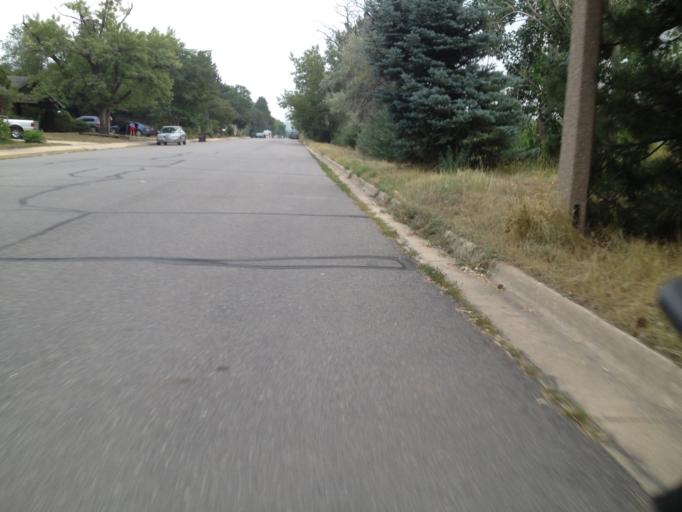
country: US
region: Colorado
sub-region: Boulder County
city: Boulder
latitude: 39.9916
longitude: -105.2430
